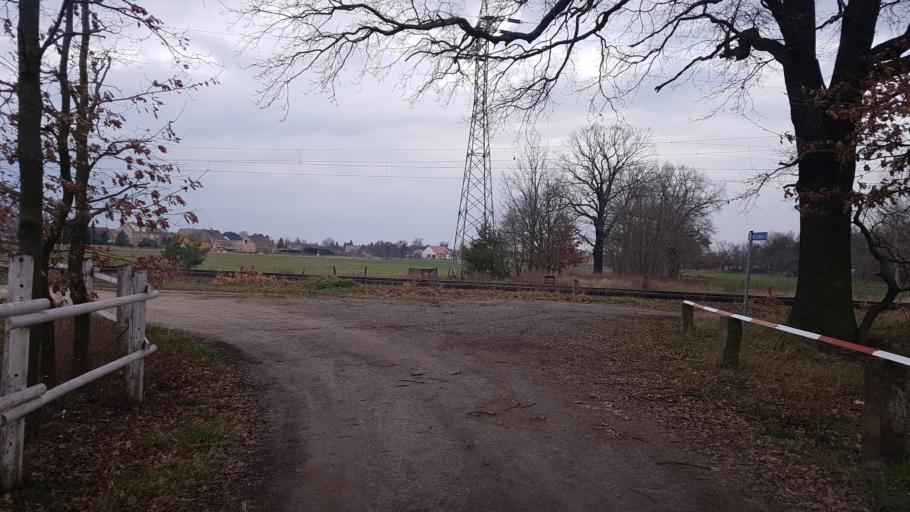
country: DE
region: Brandenburg
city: Falkenberg
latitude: 51.5852
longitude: 13.3017
